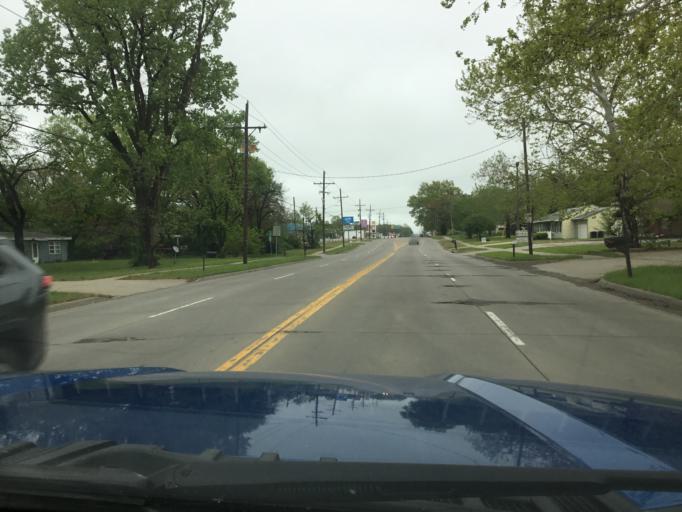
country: US
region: Kansas
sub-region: Shawnee County
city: Topeka
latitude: 39.0294
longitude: -95.7333
